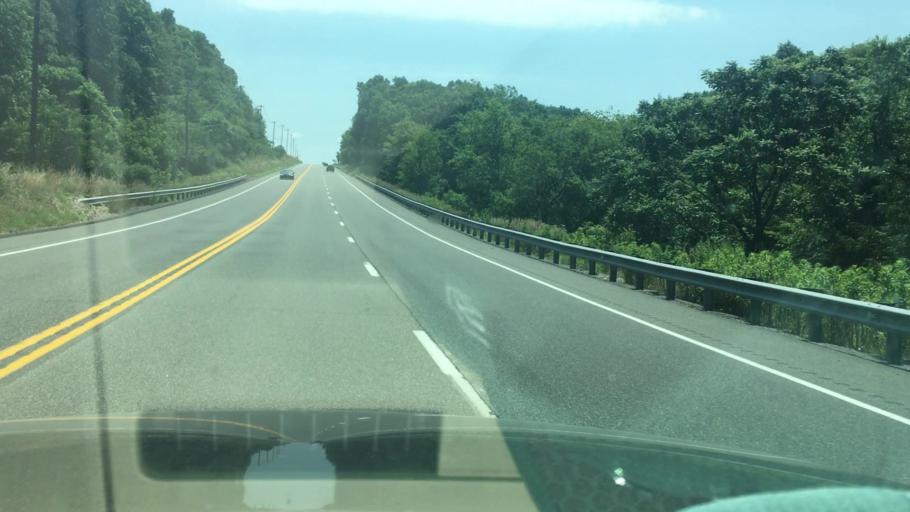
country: US
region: Pennsylvania
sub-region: Lehigh County
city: Schnecksville
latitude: 40.6248
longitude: -75.6676
